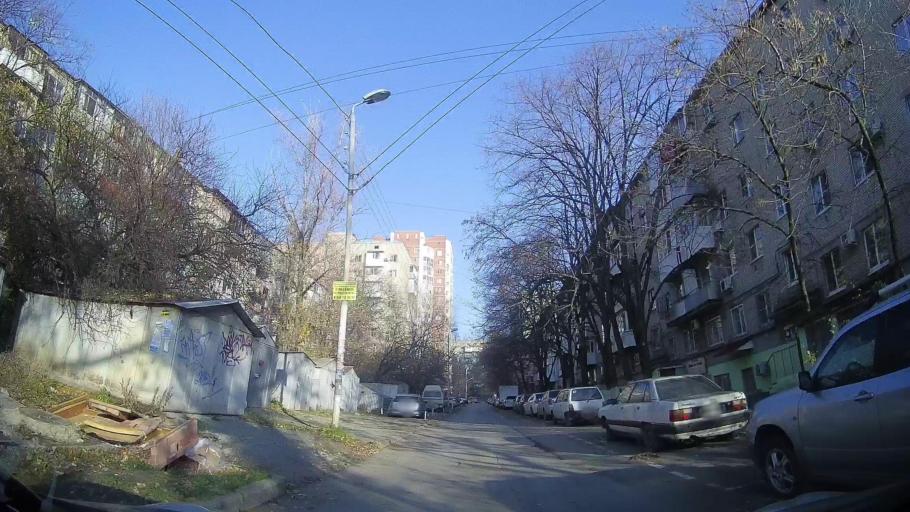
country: RU
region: Rostov
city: Rostov-na-Donu
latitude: 47.2284
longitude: 39.7103
